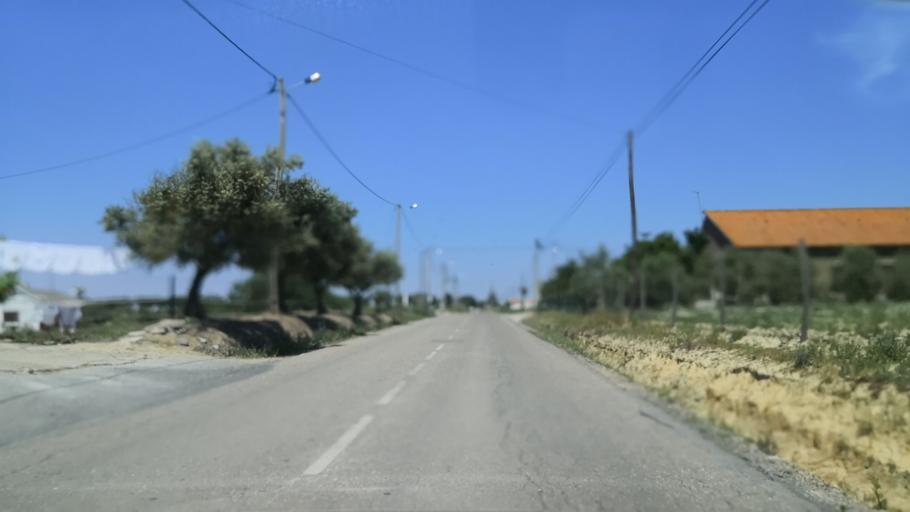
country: PT
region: Santarem
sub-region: Benavente
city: Poceirao
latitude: 38.6704
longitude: -8.7358
